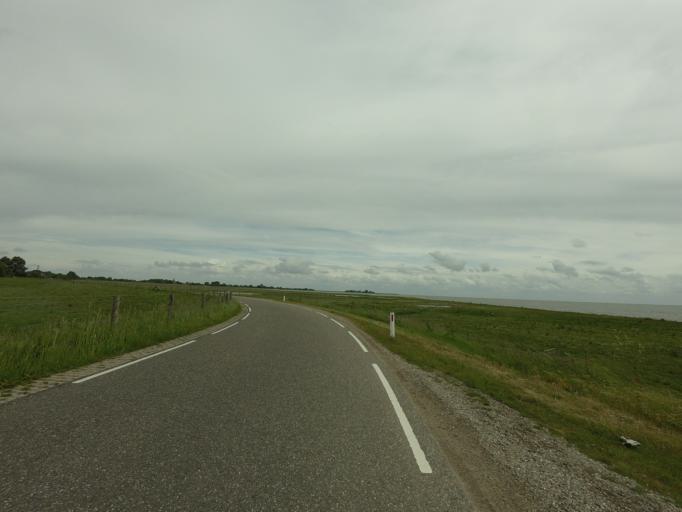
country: NL
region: North Holland
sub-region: Gemeente Hoorn
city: Hoorn
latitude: 52.6346
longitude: 5.1016
